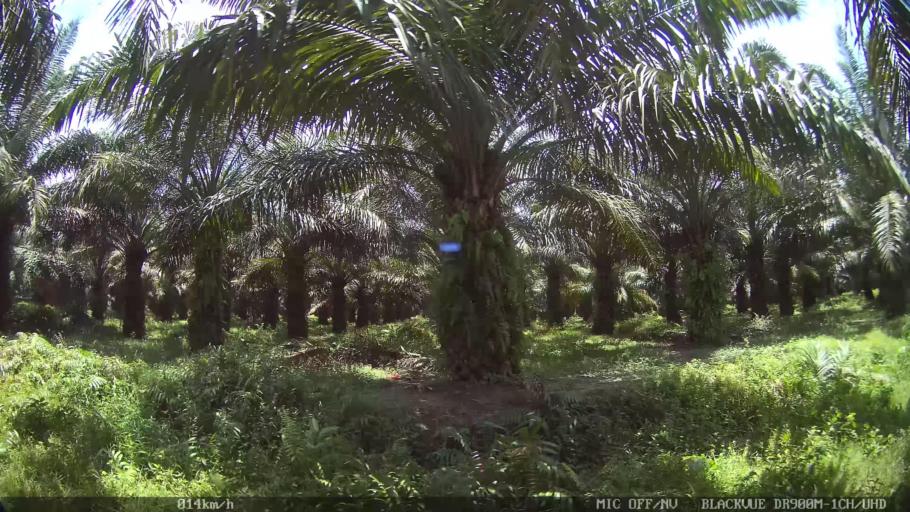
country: ID
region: North Sumatra
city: Percut
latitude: 3.5395
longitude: 98.8718
